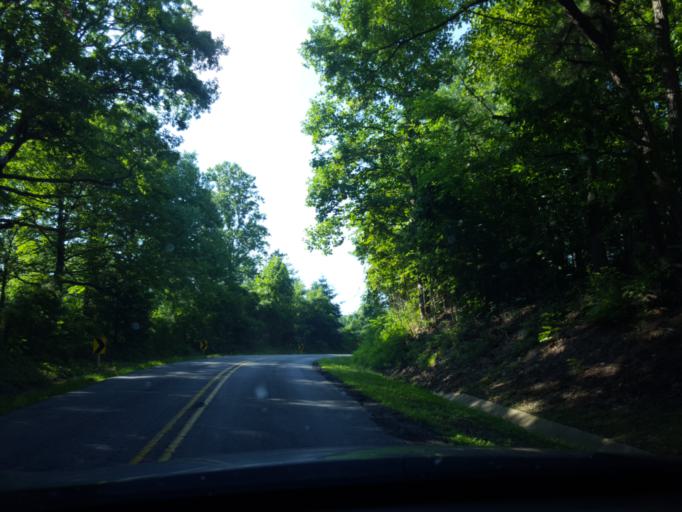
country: US
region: Virginia
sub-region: Nelson County
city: Nellysford
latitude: 37.9200
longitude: -78.9843
